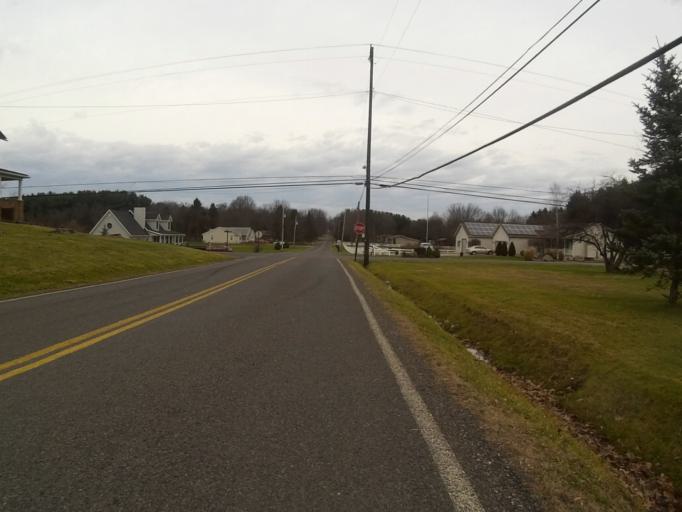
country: US
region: Ohio
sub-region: Portage County
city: Brimfield
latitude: 41.0502
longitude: -81.3289
